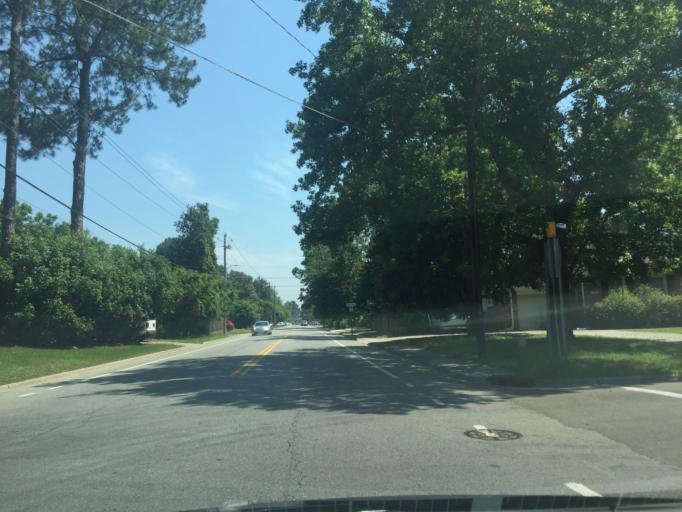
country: US
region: Georgia
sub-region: Chatham County
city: Savannah
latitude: 32.0326
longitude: -81.1042
